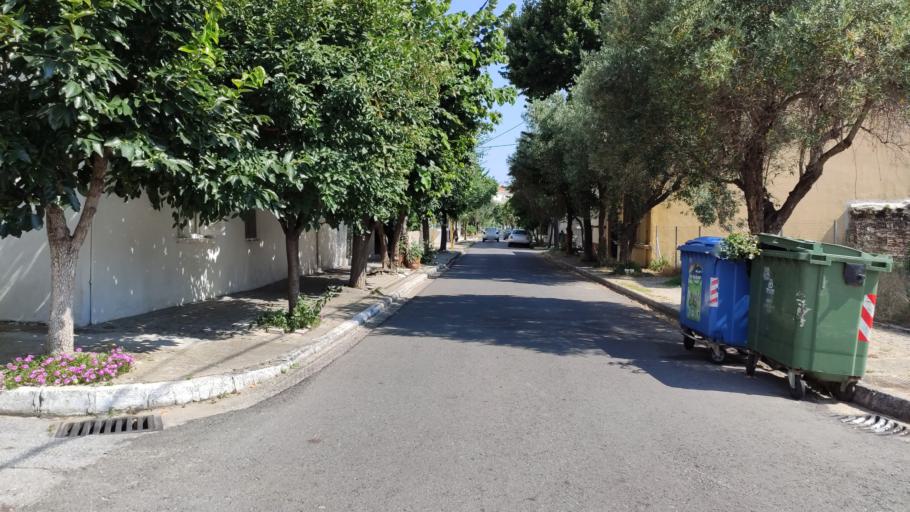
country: GR
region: East Macedonia and Thrace
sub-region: Nomos Rodopis
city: Komotini
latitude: 41.1134
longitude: 25.3929
